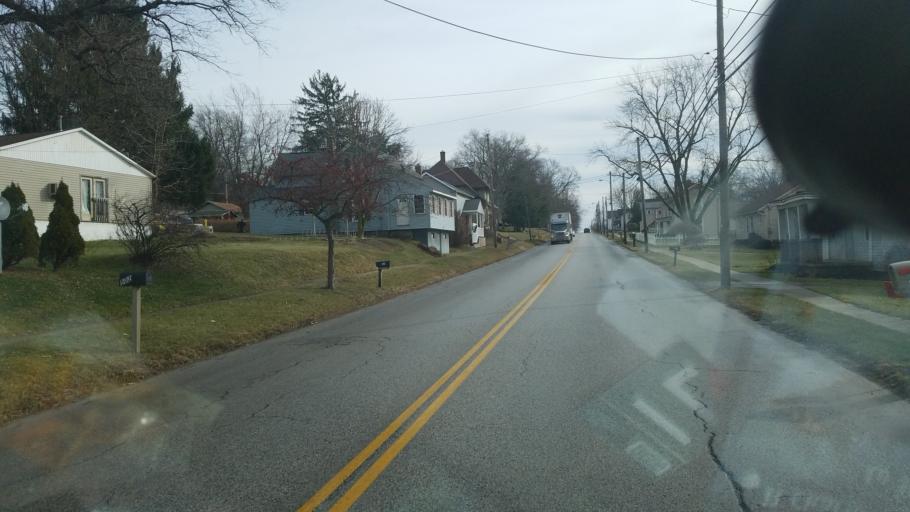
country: US
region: Ohio
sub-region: Wayne County
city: Apple Creek
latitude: 40.7543
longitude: -81.8425
